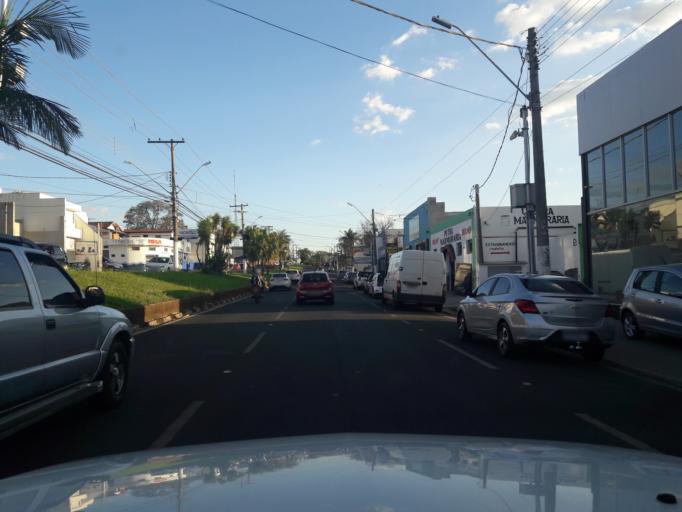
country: BR
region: Sao Paulo
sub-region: Moji-Guacu
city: Mogi-Gaucu
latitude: -22.3946
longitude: -46.9466
